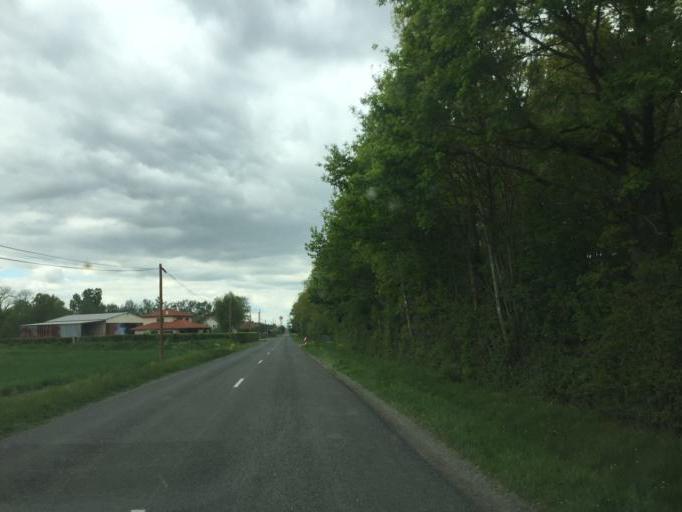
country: FR
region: Rhone-Alpes
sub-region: Departement de l'Ain
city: Amberieux-en-Dombes
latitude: 45.9810
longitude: 4.9228
